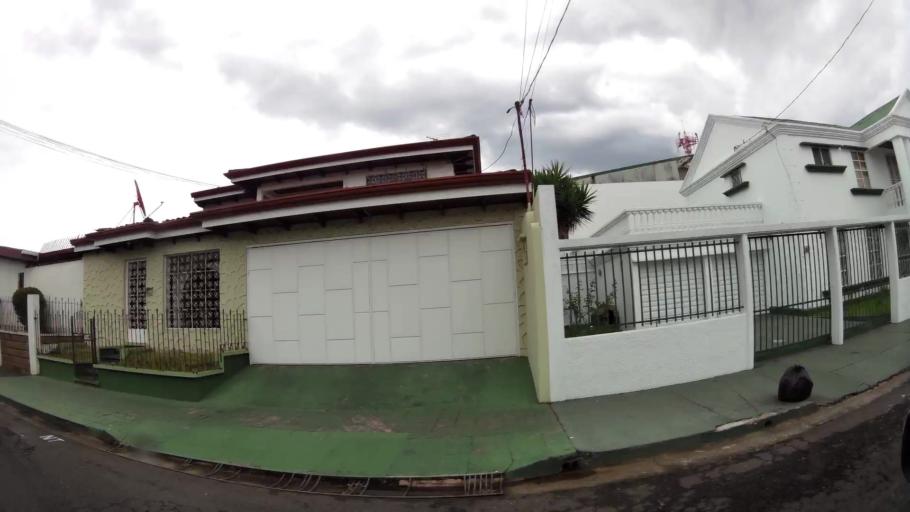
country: CR
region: San Jose
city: Calle Blancos
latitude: 9.9513
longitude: -84.0612
